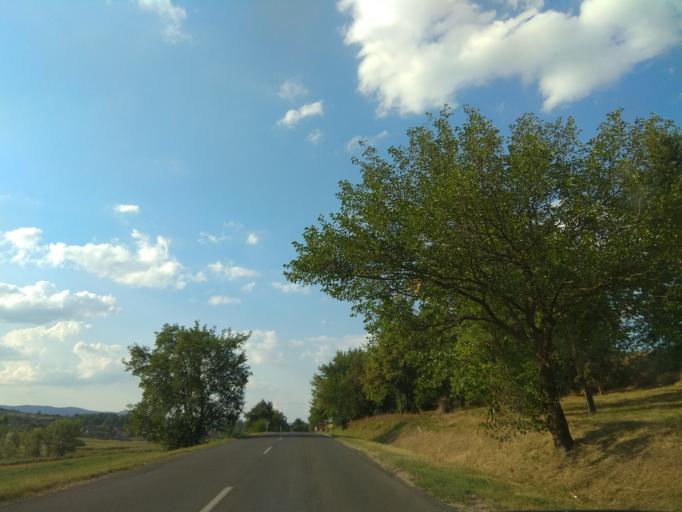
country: HU
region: Borsod-Abauj-Zemplen
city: Harsany
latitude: 47.9544
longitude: 20.7447
